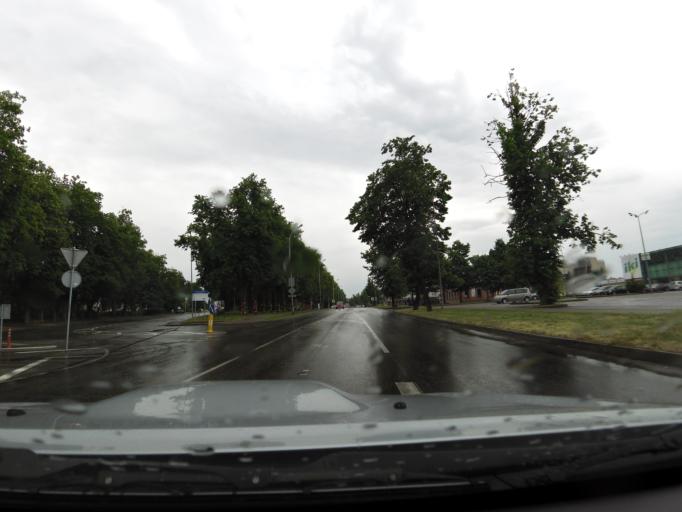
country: LT
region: Marijampoles apskritis
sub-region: Marijampole Municipality
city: Marijampole
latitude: 54.5466
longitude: 23.3473
